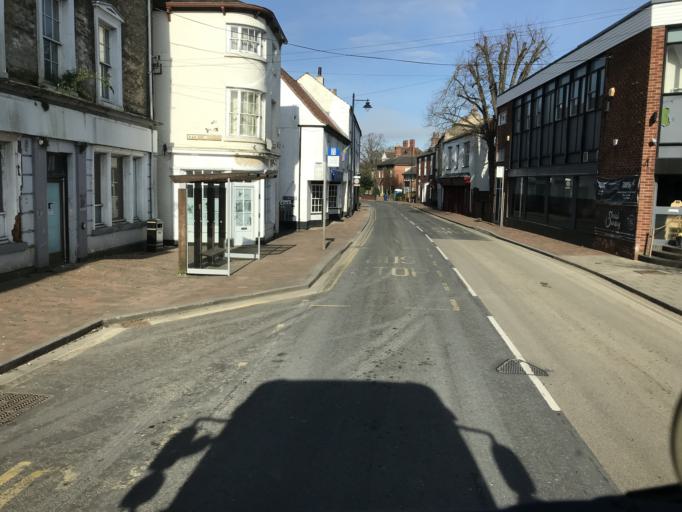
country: GB
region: England
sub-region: Lincolnshire
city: Market Rasen
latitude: 53.3877
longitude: -0.3378
